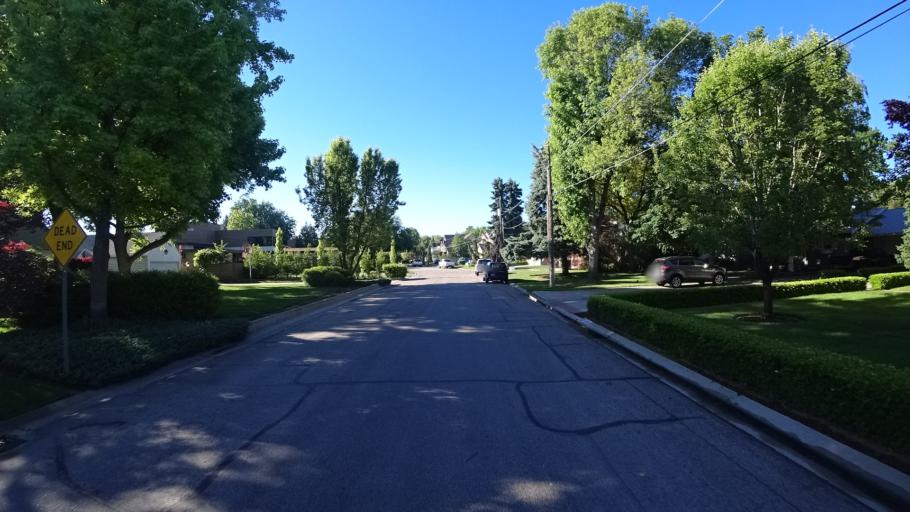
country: US
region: Idaho
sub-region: Ada County
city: Garden City
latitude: 43.6136
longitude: -116.2300
